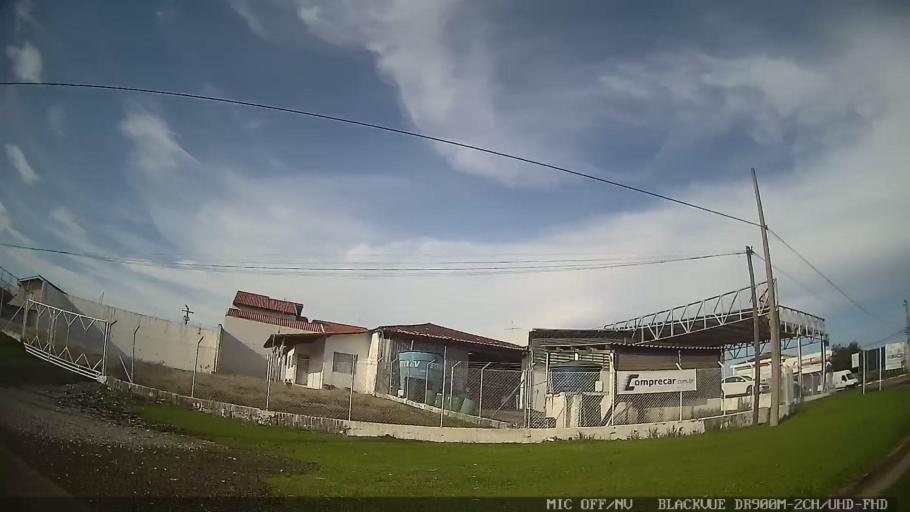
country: BR
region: Sao Paulo
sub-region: Tiete
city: Tiete
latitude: -23.1177
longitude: -47.7118
